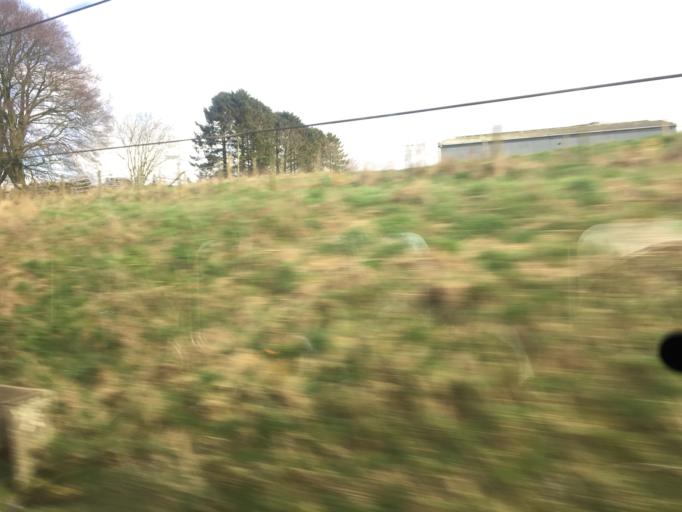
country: GB
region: Scotland
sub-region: Dumfries and Galloway
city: Moffat
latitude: 55.2784
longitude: -3.4212
